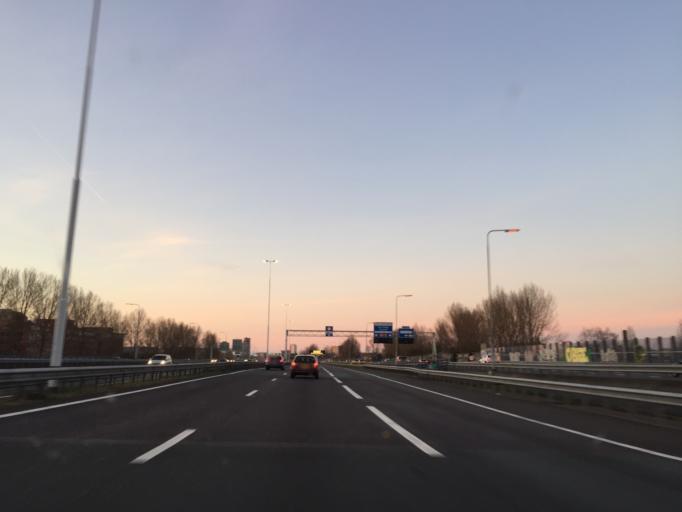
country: NL
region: South Holland
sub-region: Gemeente Rotterdam
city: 's-Gravenland
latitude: 51.9211
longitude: 4.5355
